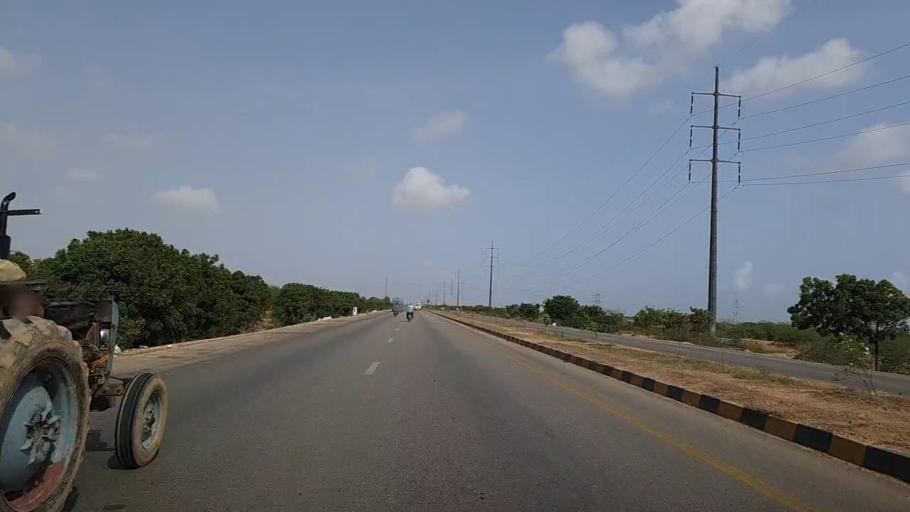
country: PK
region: Sindh
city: Gharo
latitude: 24.8274
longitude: 67.4709
